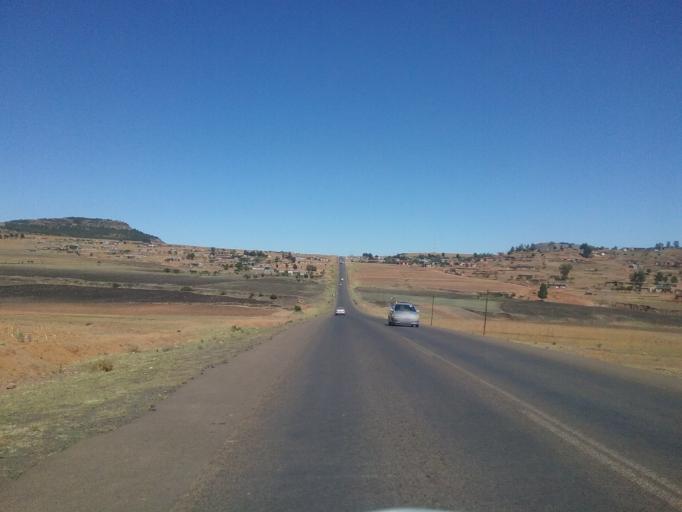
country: LS
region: Quthing
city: Quthing
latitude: -30.3967
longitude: 27.6480
